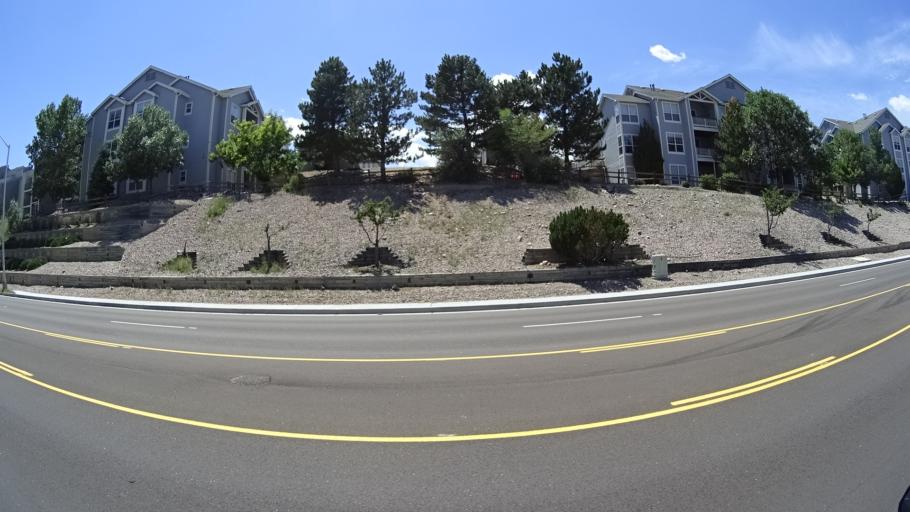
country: US
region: Colorado
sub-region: El Paso County
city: Air Force Academy
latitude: 38.9178
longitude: -104.8351
